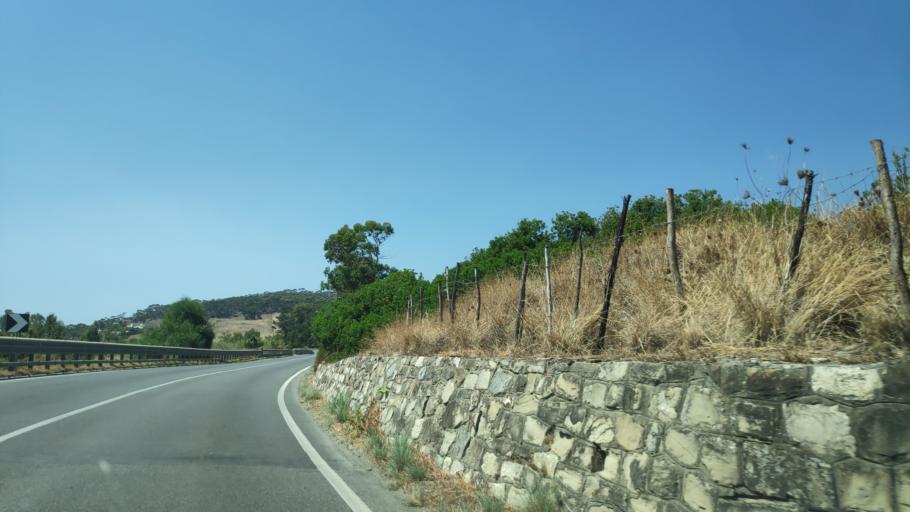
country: IT
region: Calabria
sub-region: Provincia di Reggio Calabria
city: Brancaleone-Marina
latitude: 38.0022
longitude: 16.1258
